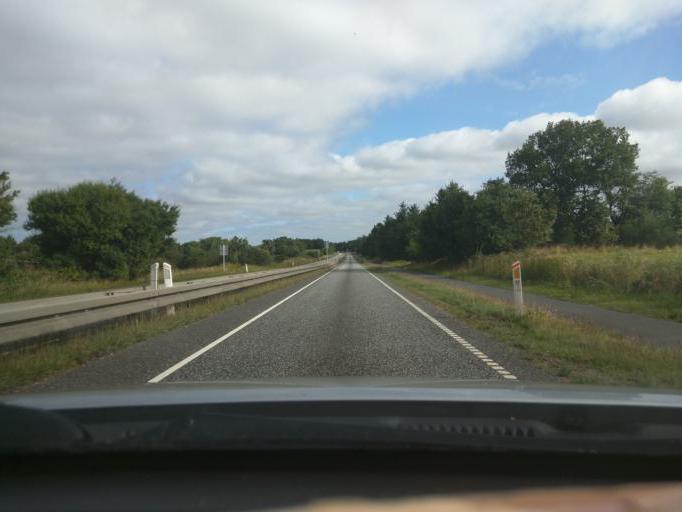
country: DK
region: Central Jutland
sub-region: Viborg Kommune
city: Viborg
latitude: 56.4198
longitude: 9.3841
